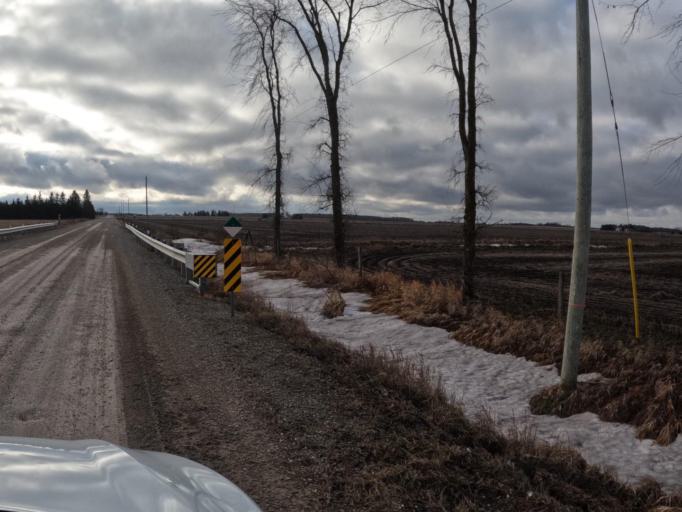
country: CA
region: Ontario
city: Shelburne
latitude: 43.8929
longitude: -80.3607
